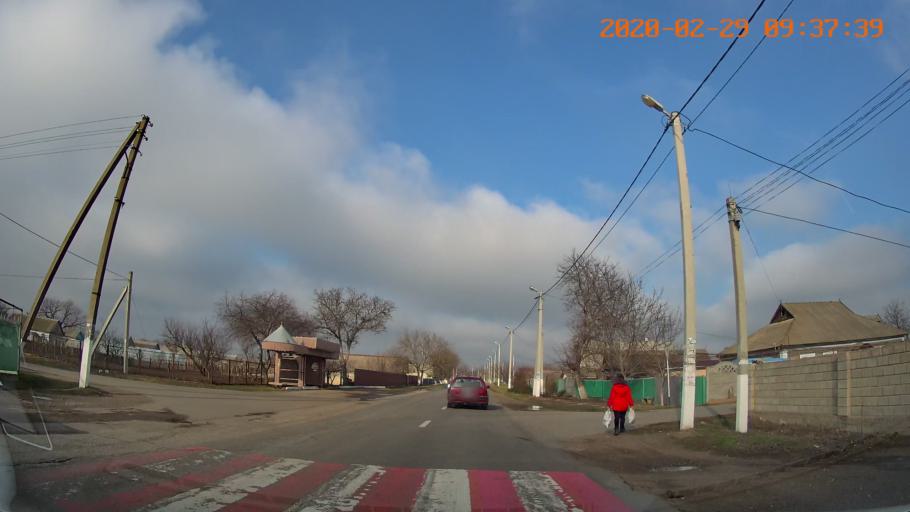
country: MD
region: Telenesti
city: Dnestrovsc
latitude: 46.6283
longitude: 29.8749
